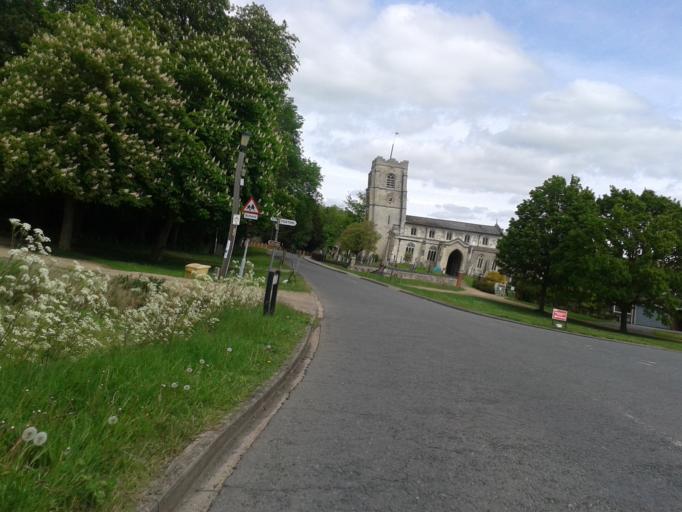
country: GB
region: England
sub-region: Cambridgeshire
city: Haslingfield
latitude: 52.1293
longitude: 0.0383
